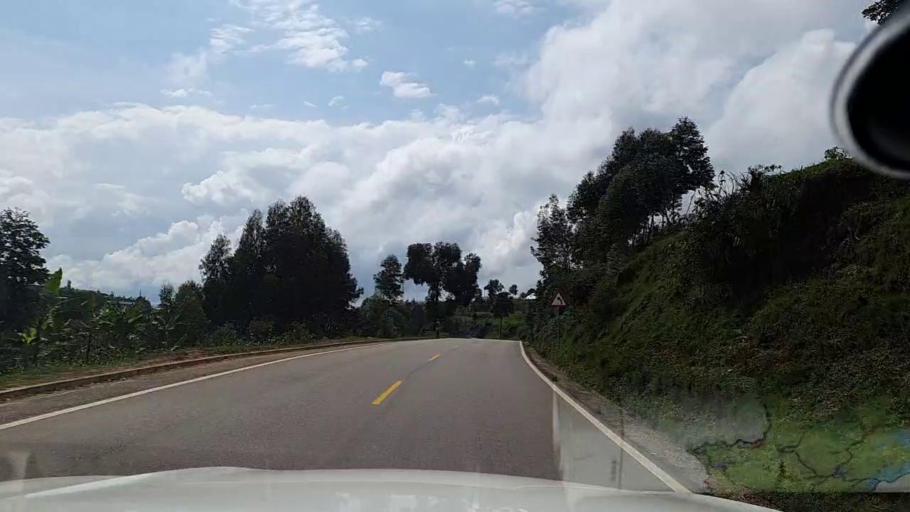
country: RW
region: Southern Province
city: Nzega
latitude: -2.4993
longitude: 29.5077
